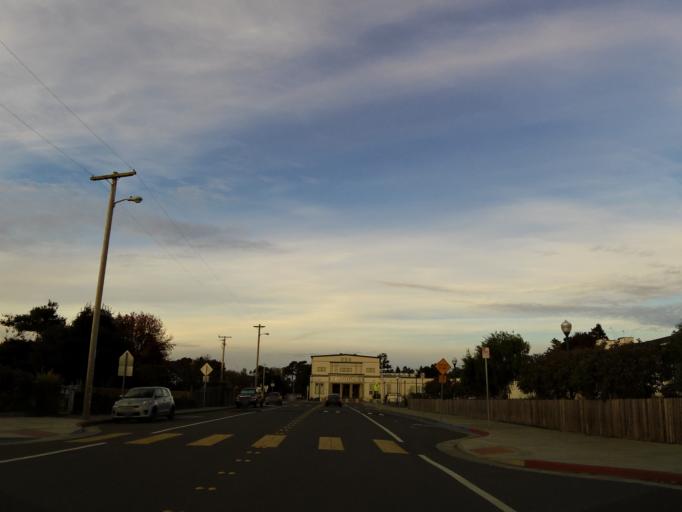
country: US
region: California
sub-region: Mendocino County
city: Fort Bragg
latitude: 39.4473
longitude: -123.7980
